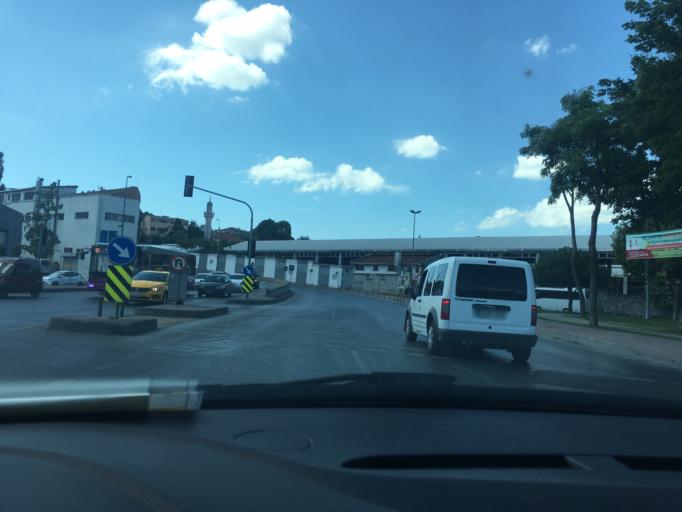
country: TR
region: Istanbul
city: Eminoenue
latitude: 41.0303
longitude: 28.9677
